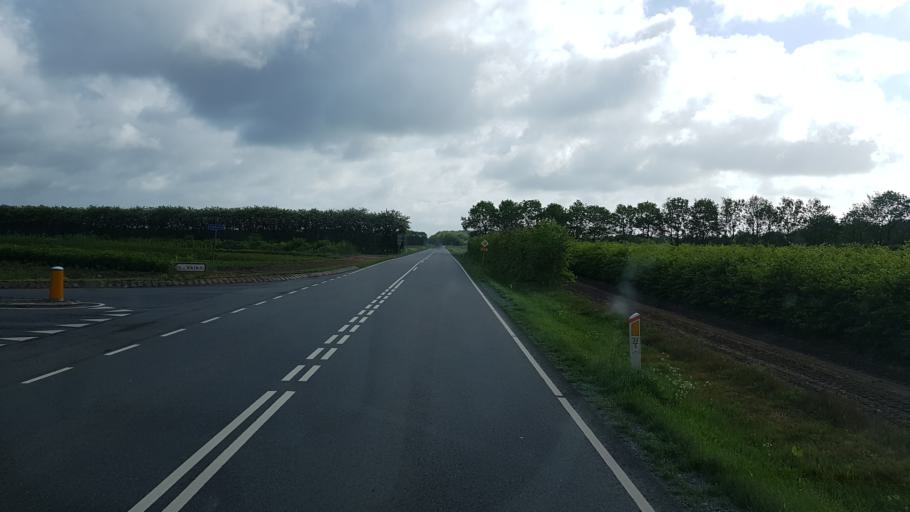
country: DK
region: South Denmark
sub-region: Vejen Kommune
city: Vejen
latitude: 55.4553
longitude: 9.1579
